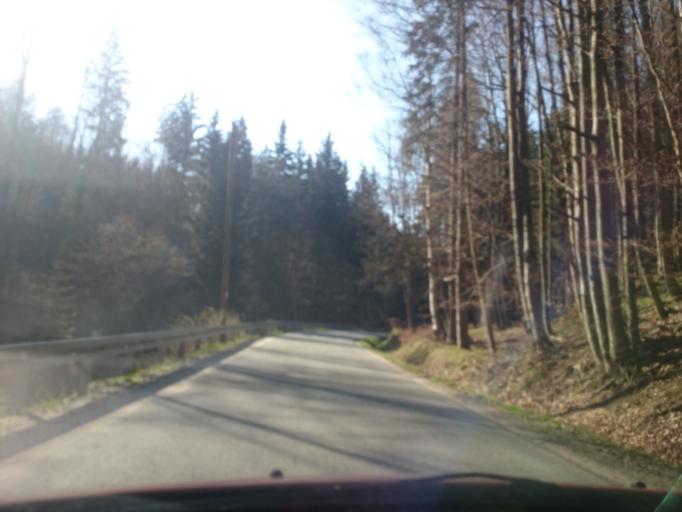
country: PL
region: Lower Silesian Voivodeship
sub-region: Powiat klodzki
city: Duszniki-Zdroj
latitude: 50.3386
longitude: 16.4045
